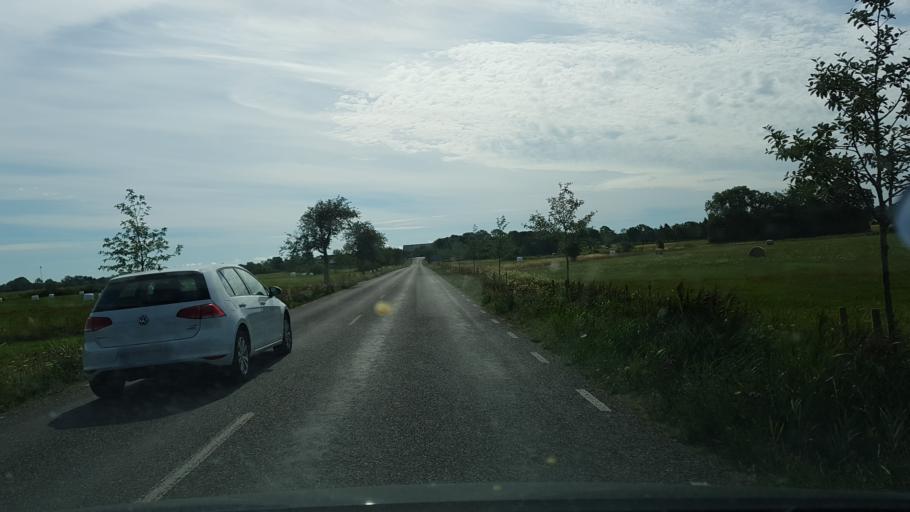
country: SE
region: Gotland
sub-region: Gotland
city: Hemse
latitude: 57.4314
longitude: 18.6217
